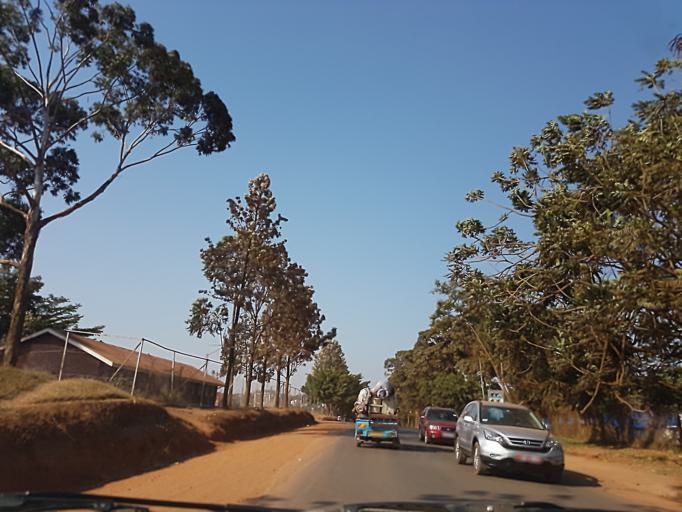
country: UG
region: Central Region
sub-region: Wakiso District
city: Kireka
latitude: 0.3385
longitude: 32.6150
